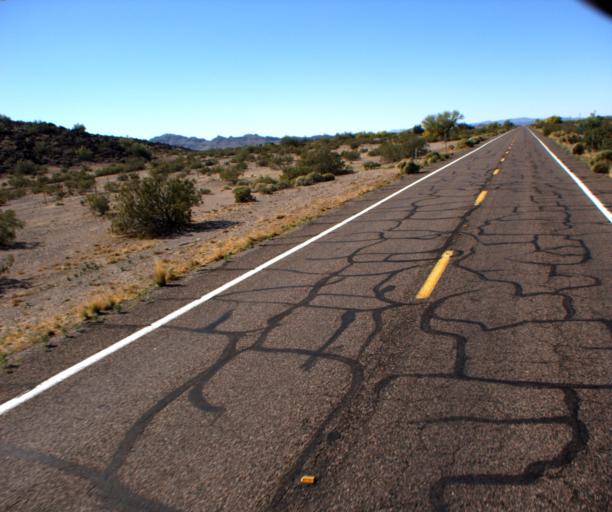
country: US
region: Arizona
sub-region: Maricopa County
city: Gila Bend
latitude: 32.7538
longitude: -112.8250
